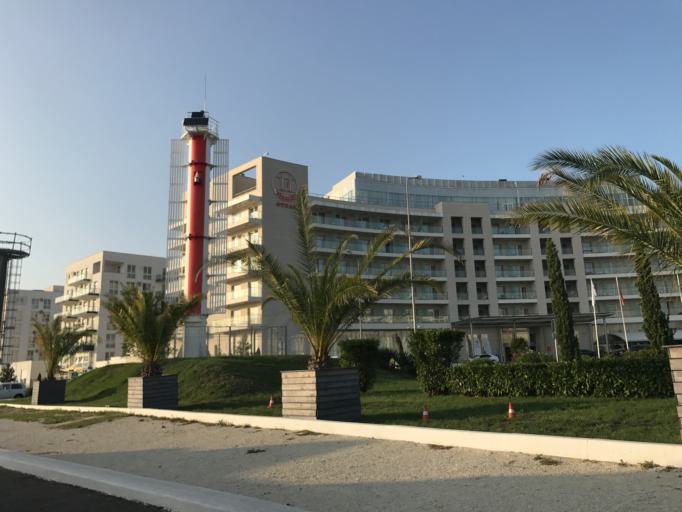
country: RU
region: Krasnodarskiy
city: Adler
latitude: 43.4106
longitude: 39.9356
